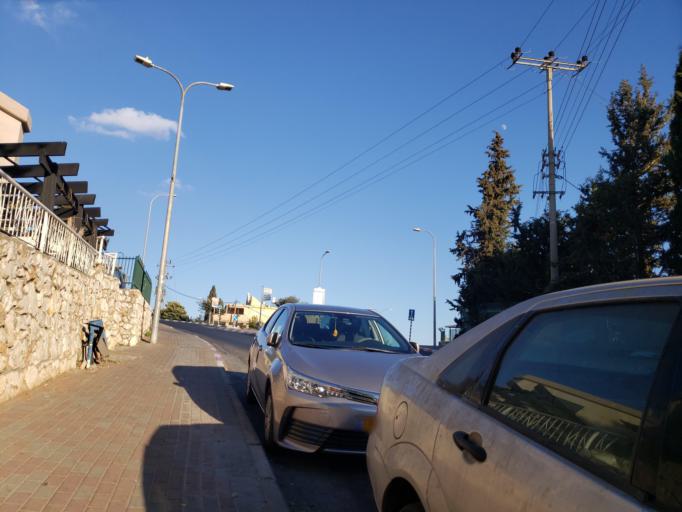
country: IL
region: Northern District
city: Safed
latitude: 32.9571
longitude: 35.4946
